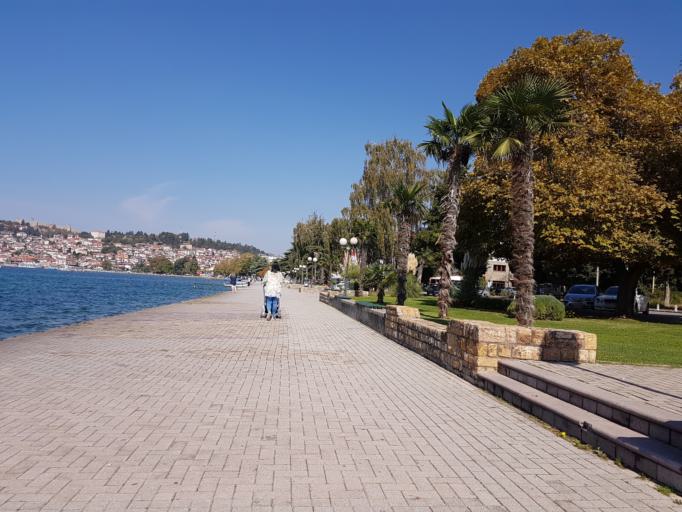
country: MK
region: Ohrid
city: Ohrid
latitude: 41.1079
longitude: 20.8062
